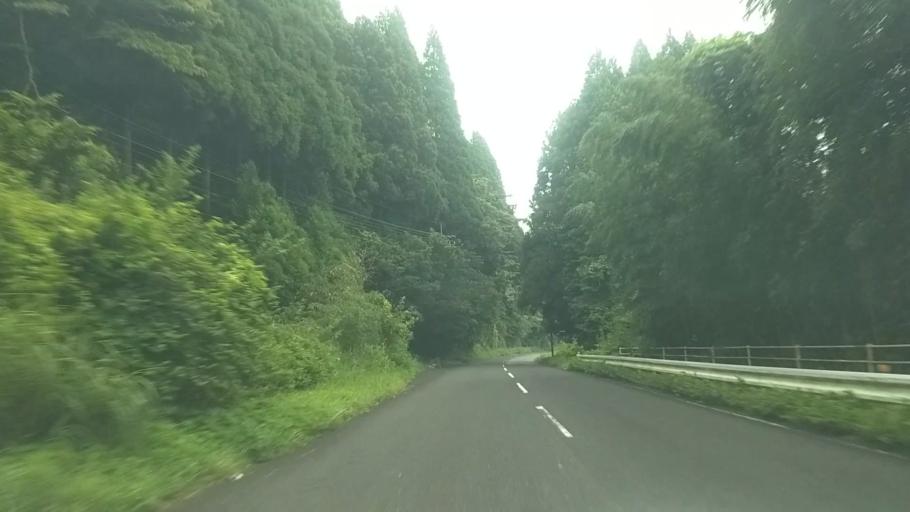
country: JP
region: Chiba
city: Katsuura
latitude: 35.2544
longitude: 140.2443
